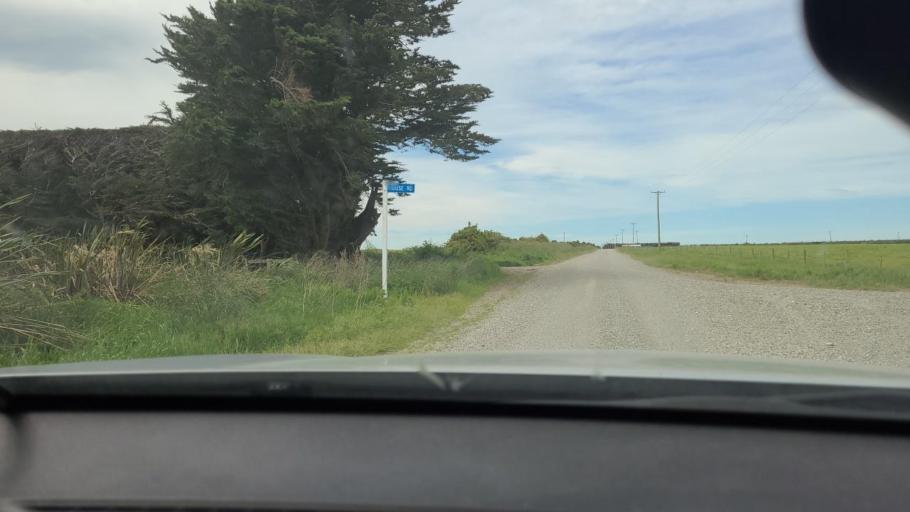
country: NZ
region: Southland
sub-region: Southland District
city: Riverton
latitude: -46.3325
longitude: 168.1786
